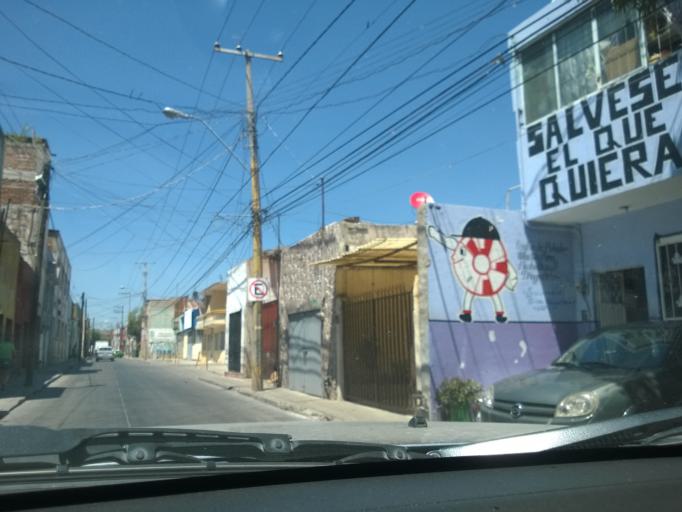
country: MX
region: Guanajuato
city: Leon
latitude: 21.1178
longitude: -101.6778
